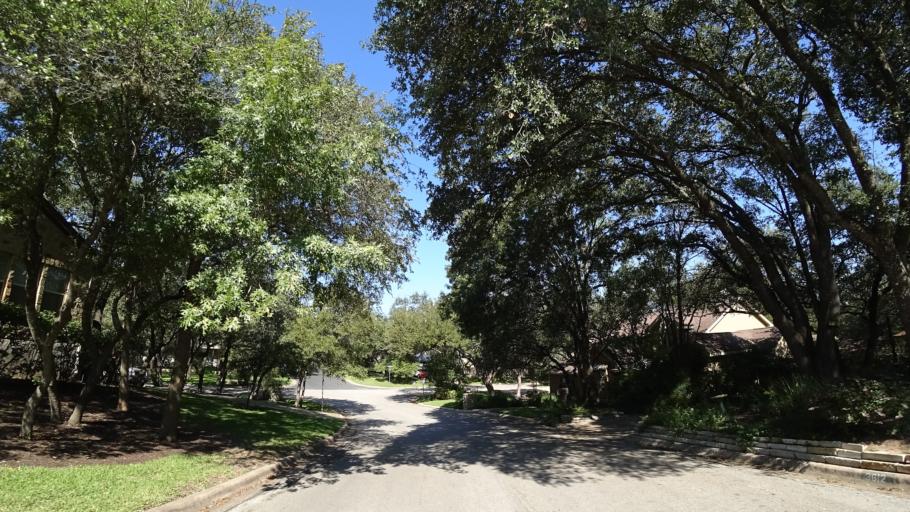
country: US
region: Texas
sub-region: Travis County
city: Rollingwood
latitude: 30.2746
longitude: -97.8096
